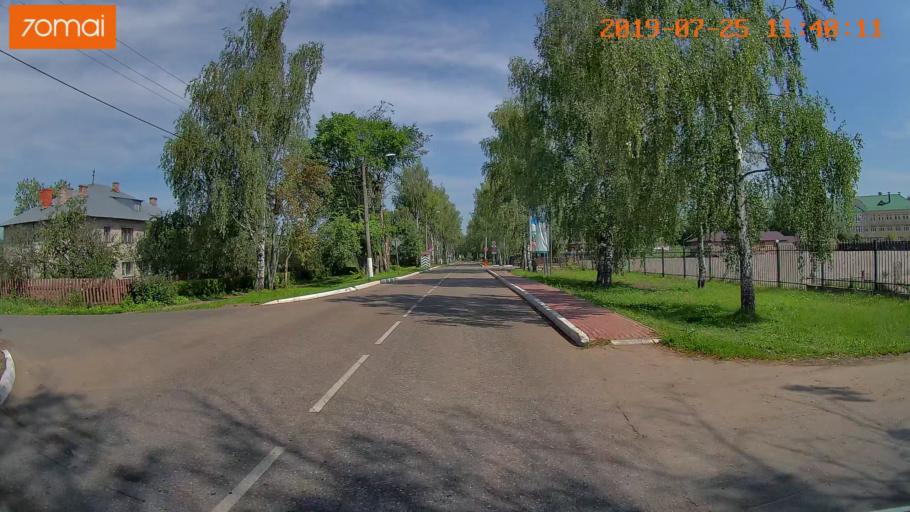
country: RU
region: Ivanovo
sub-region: Privolzhskiy Rayon
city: Ples
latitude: 57.4522
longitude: 41.5049
